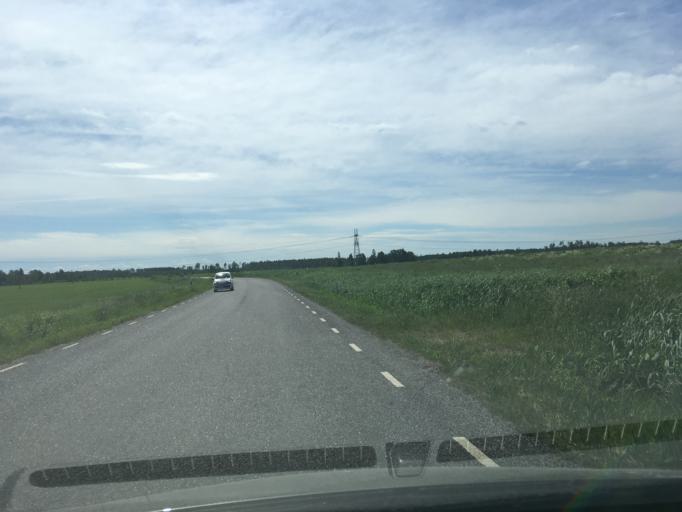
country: EE
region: Paernumaa
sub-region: Audru vald
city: Audru
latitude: 58.4381
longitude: 24.3971
